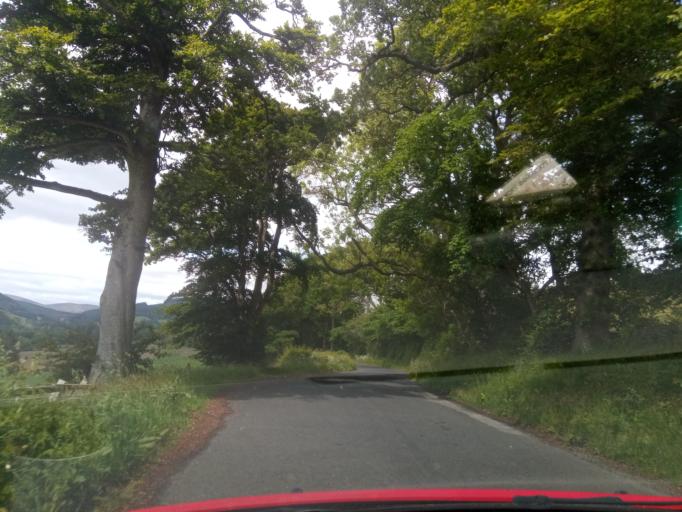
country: GB
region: Scotland
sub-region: The Scottish Borders
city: Selkirk
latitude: 55.5835
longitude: -2.8350
